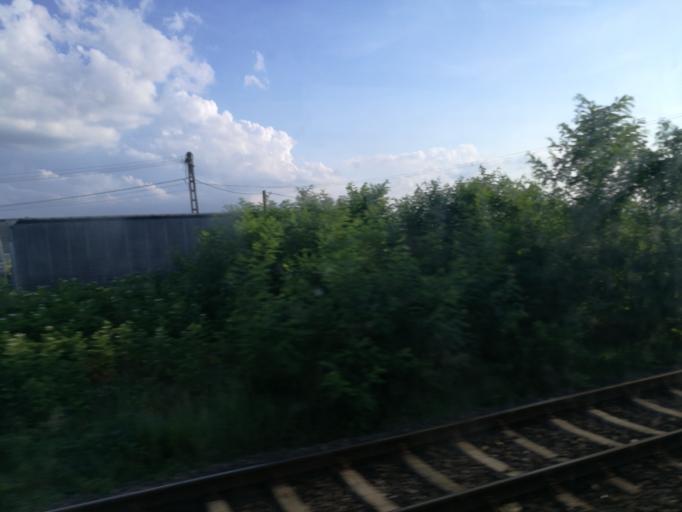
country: RO
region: Arges
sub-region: Comuna Calinesti
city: Calinesti
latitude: 44.8089
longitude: 25.0662
